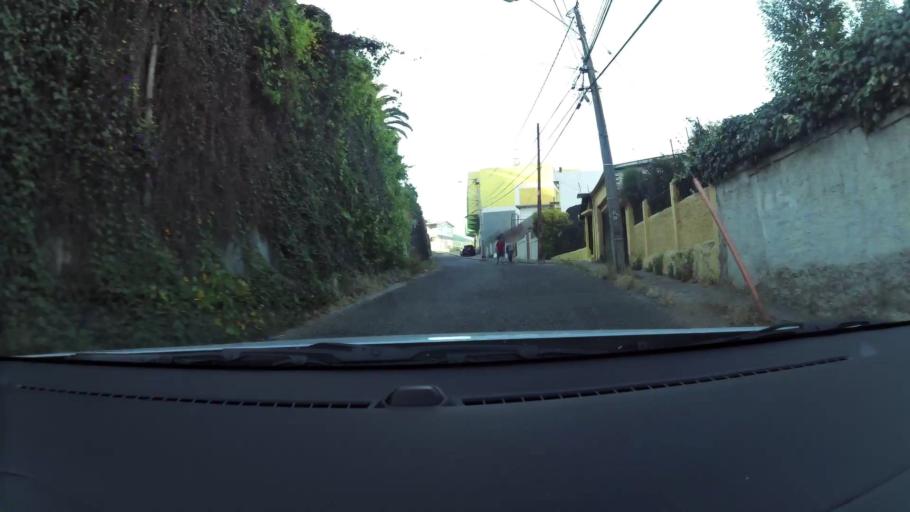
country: CL
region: Valparaiso
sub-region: Provincia de Valparaiso
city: Valparaiso
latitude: -33.0511
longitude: -71.6233
